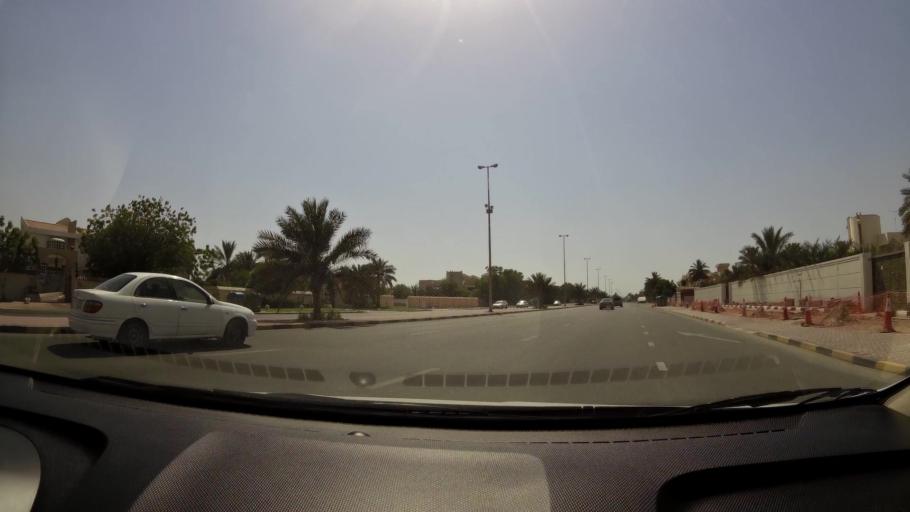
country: AE
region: Ajman
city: Ajman
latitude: 25.4042
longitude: 55.4759
